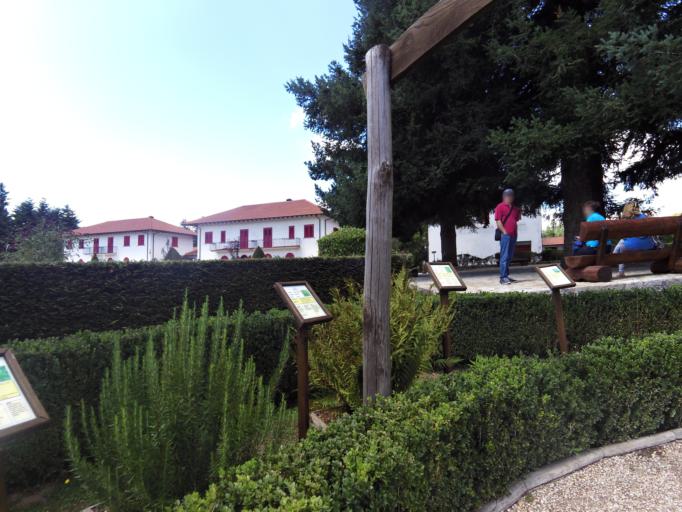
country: IT
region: Calabria
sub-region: Provincia di Vibo-Valentia
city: Mongiana
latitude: 38.5157
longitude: 16.3164
